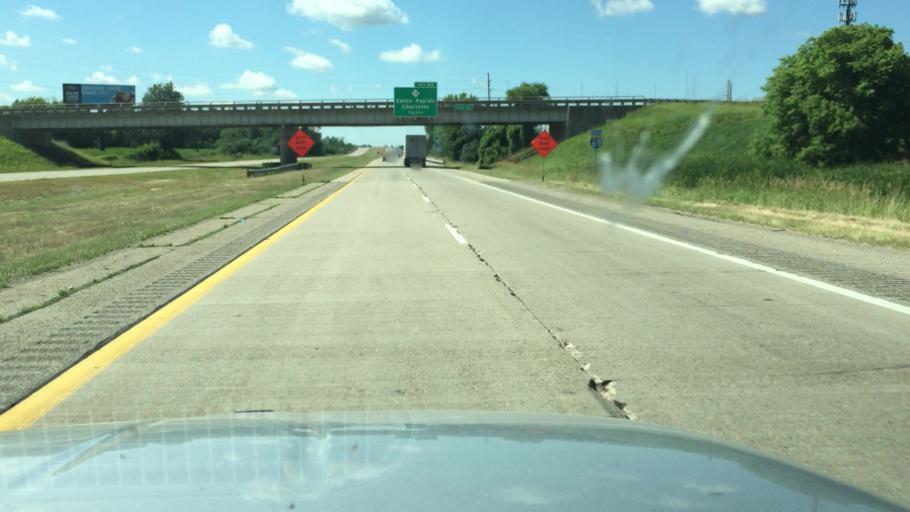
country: US
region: Michigan
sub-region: Eaton County
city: Charlotte
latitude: 42.5691
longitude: -84.8212
